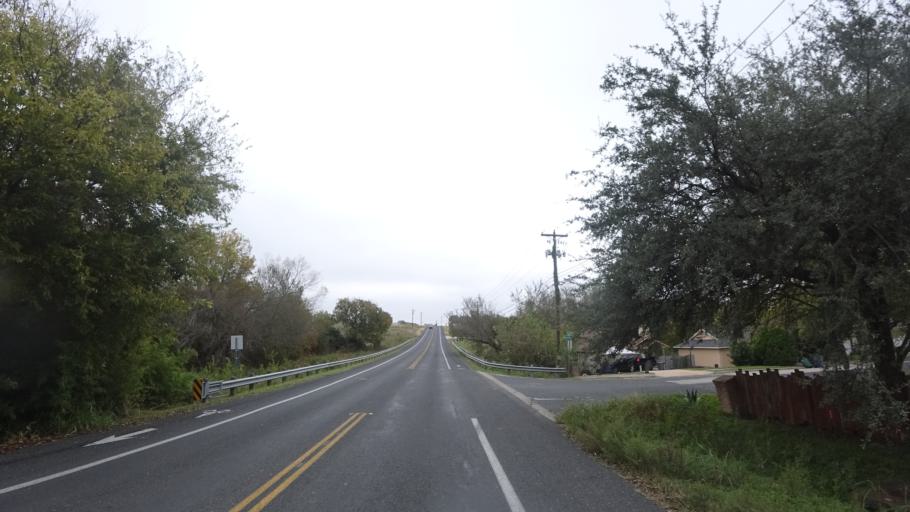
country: US
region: Texas
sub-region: Travis County
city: Pflugerville
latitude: 30.3888
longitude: -97.6550
